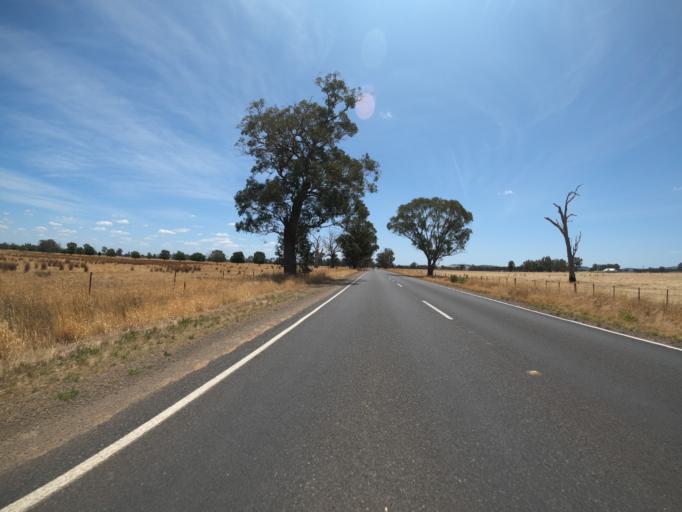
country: AU
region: Victoria
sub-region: Benalla
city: Benalla
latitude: -36.5150
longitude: 146.0313
